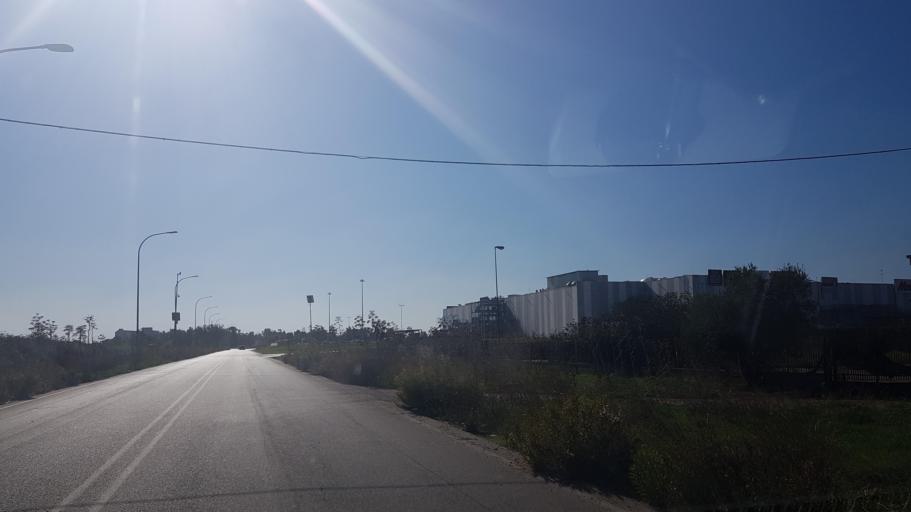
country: IT
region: Apulia
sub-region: Provincia di Foggia
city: Carapelle
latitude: 41.4171
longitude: 15.6551
